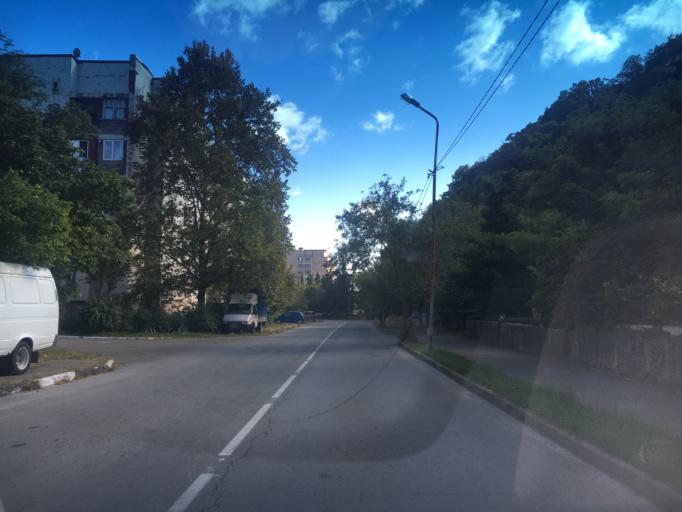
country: RU
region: Krasnodarskiy
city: Nebug
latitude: 44.1818
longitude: 38.9733
